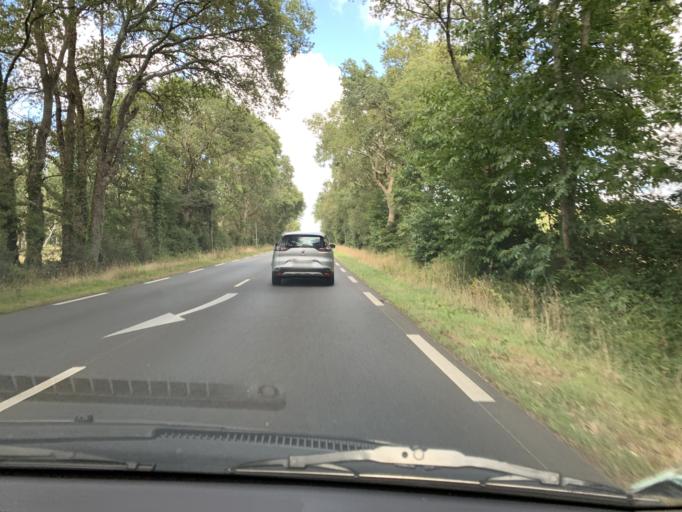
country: FR
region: Pays de la Loire
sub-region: Departement de la Loire-Atlantique
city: Saint-Molf
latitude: 47.3844
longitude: -2.3804
